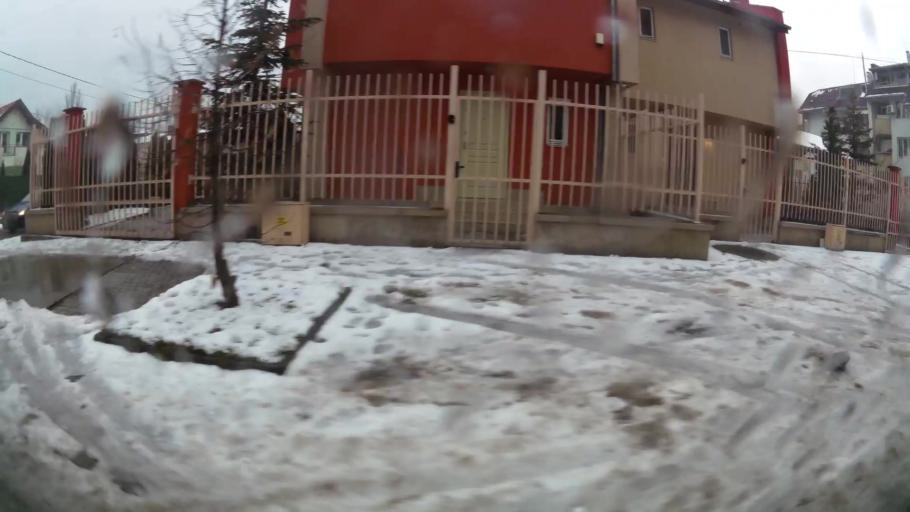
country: BG
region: Sofia-Capital
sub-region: Stolichna Obshtina
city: Sofia
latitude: 42.6819
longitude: 23.2665
